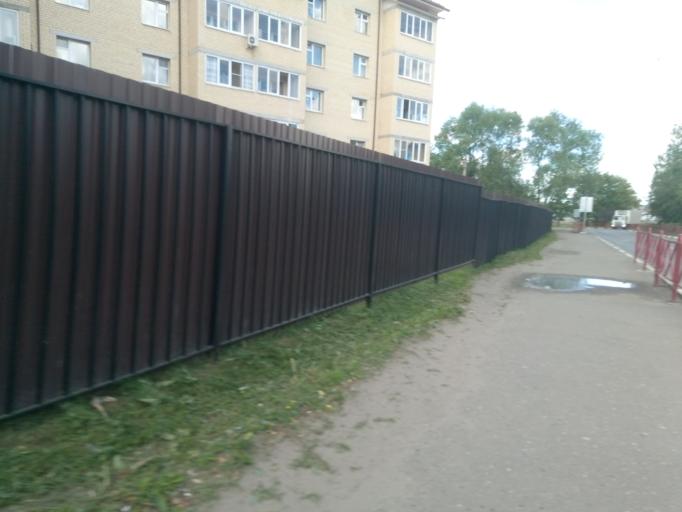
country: RU
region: Jaroslavl
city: Yaroslavl
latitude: 57.6576
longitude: 39.9562
